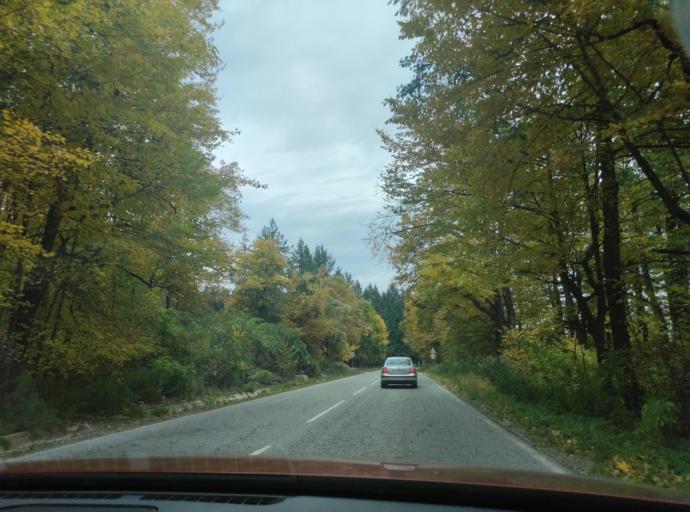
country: BG
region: Montana
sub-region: Obshtina Berkovitsa
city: Berkovitsa
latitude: 43.1788
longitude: 23.1556
